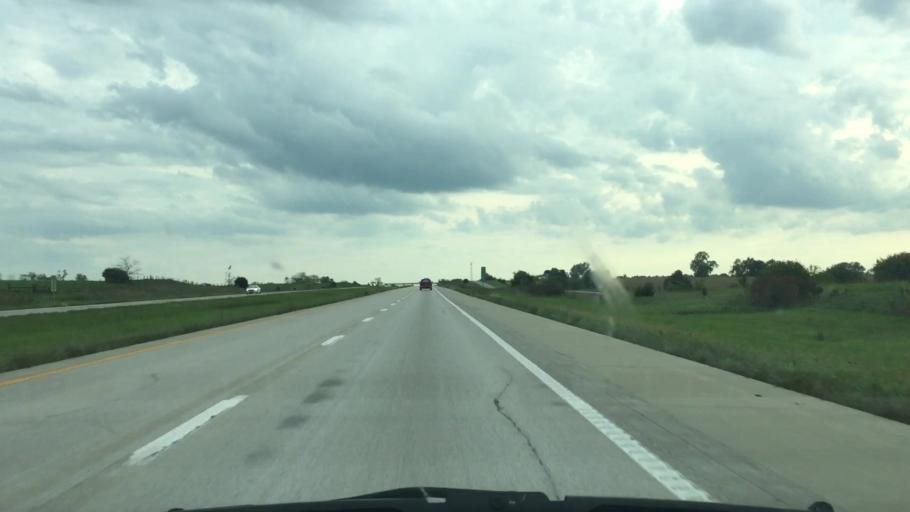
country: US
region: Missouri
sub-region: Clinton County
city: Lathrop
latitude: 39.5944
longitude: -94.2555
